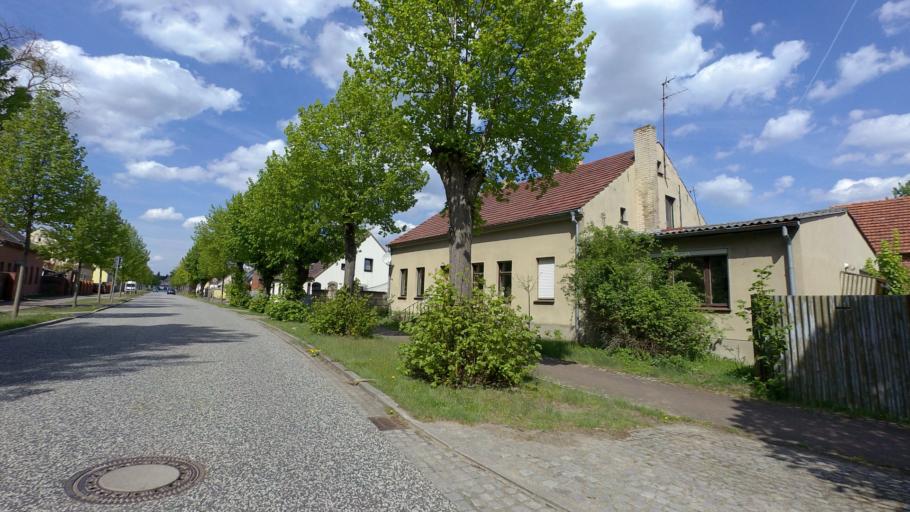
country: DE
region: Brandenburg
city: Marienwerder
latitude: 52.9016
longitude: 13.5358
